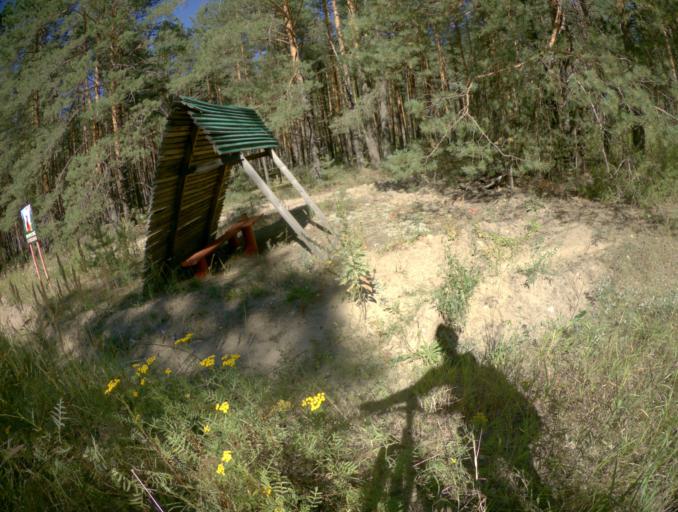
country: RU
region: Vladimir
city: Zolotkovo
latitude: 55.6235
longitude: 40.9581
